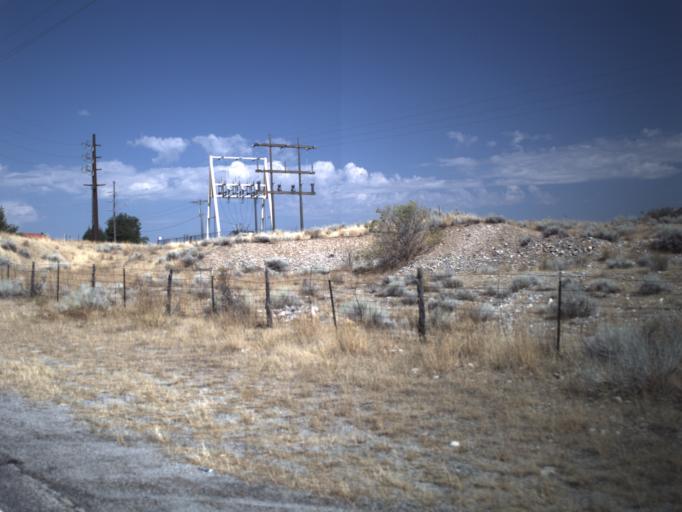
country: US
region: Utah
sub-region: Cache County
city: Hyrum
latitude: 41.6329
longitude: -111.8130
